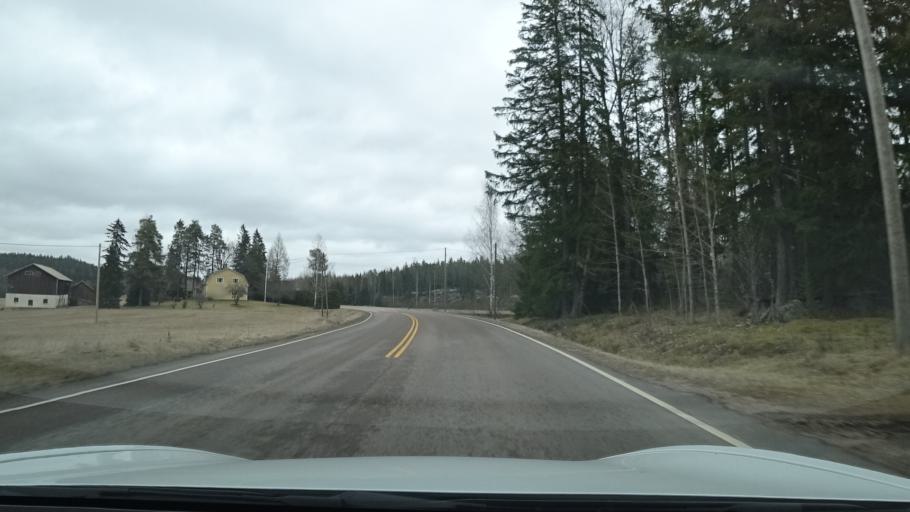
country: FI
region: Uusimaa
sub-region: Porvoo
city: Myrskylae
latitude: 60.7137
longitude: 25.9484
